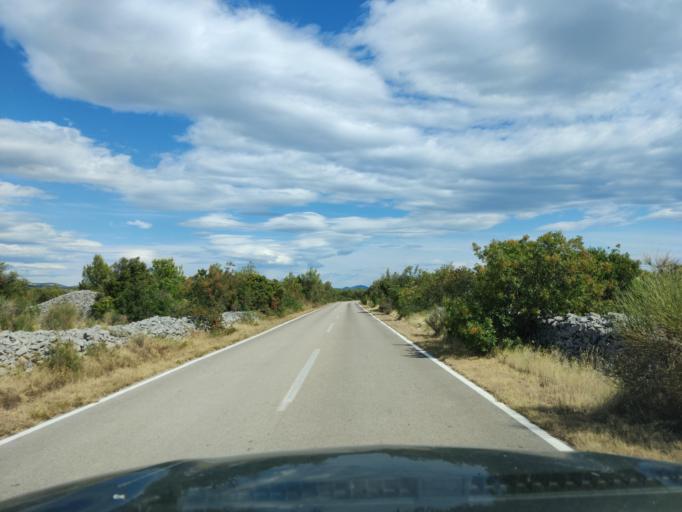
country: HR
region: Sibensko-Kniniska
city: Zaton
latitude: 43.7507
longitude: 15.8402
